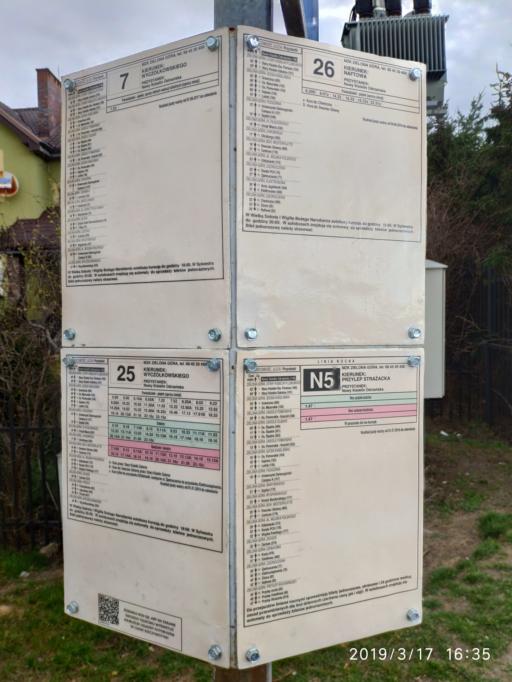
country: PL
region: Lubusz
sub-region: Zielona Gora
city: Zielona Gora
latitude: 51.9341
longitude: 15.5946
